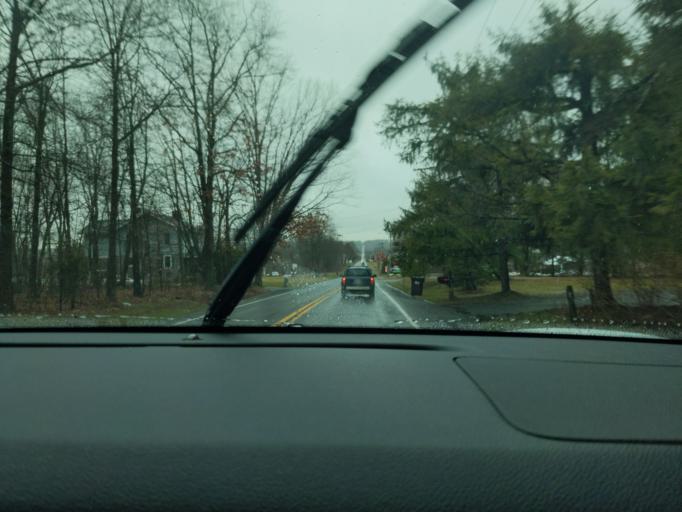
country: US
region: Pennsylvania
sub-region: Bucks County
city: Dublin
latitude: 40.3922
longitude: -75.2355
